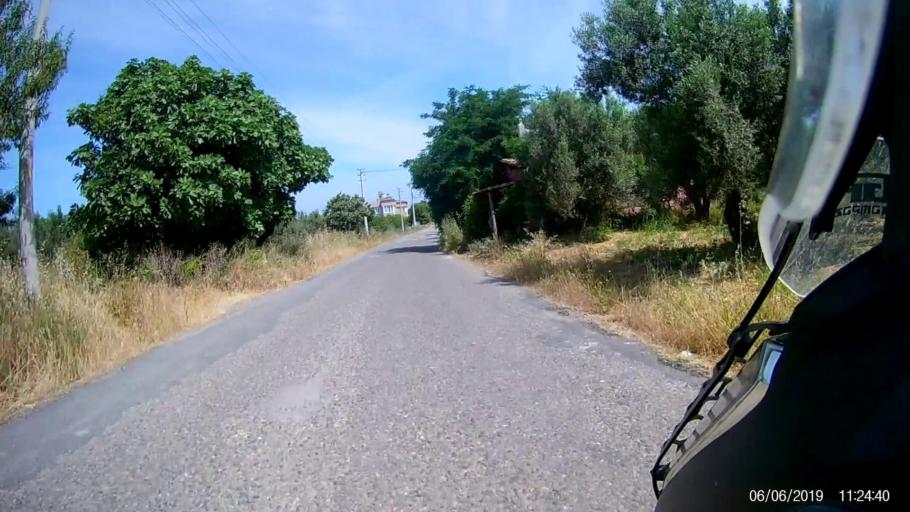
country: TR
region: Canakkale
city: Gulpinar
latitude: 39.6250
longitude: 26.1792
